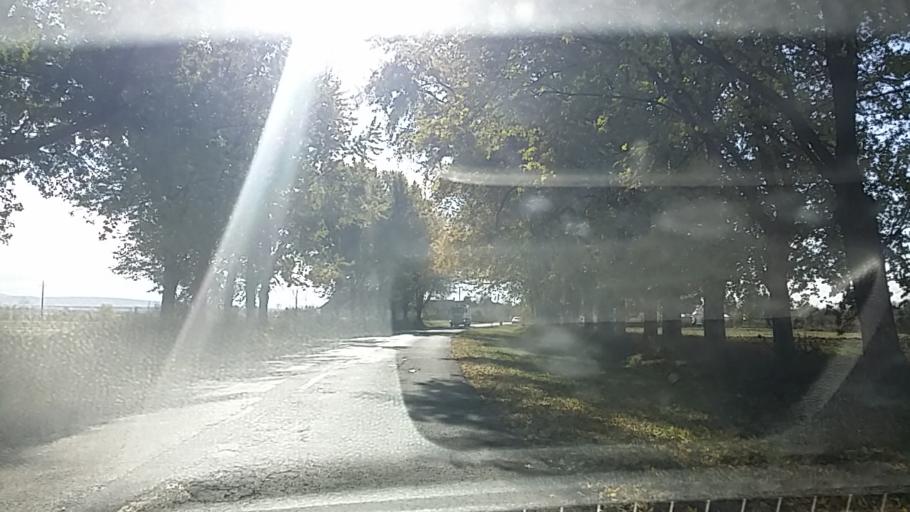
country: HU
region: Borsod-Abauj-Zemplen
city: Gonc
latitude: 48.4262
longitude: 21.2373
